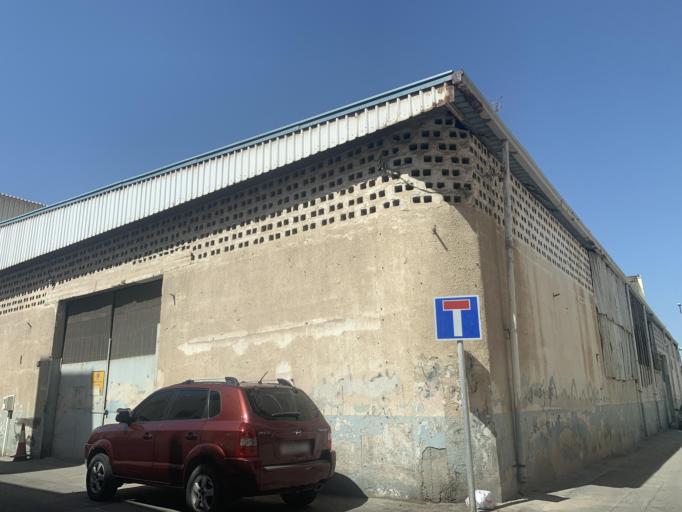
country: BH
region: Manama
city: Jidd Hafs
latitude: 26.2133
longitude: 50.5650
